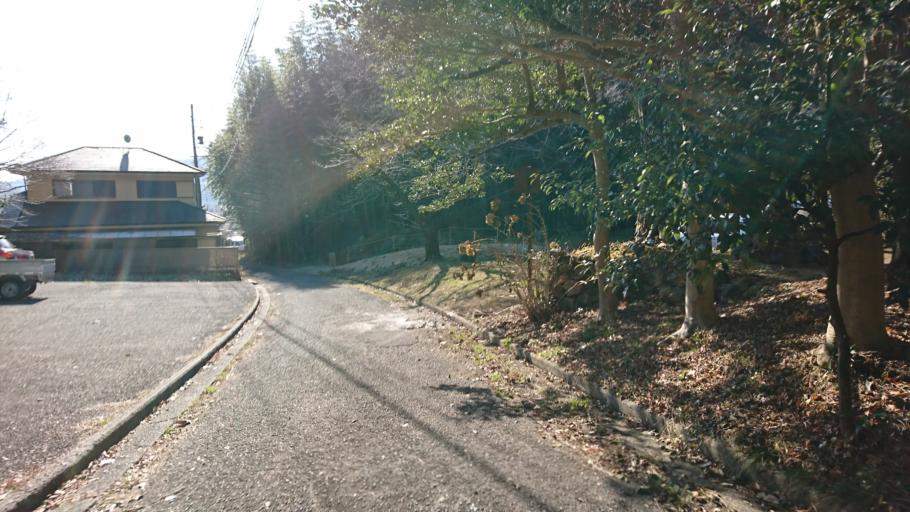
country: JP
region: Hyogo
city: Kakogawacho-honmachi
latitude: 34.8312
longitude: 134.8461
